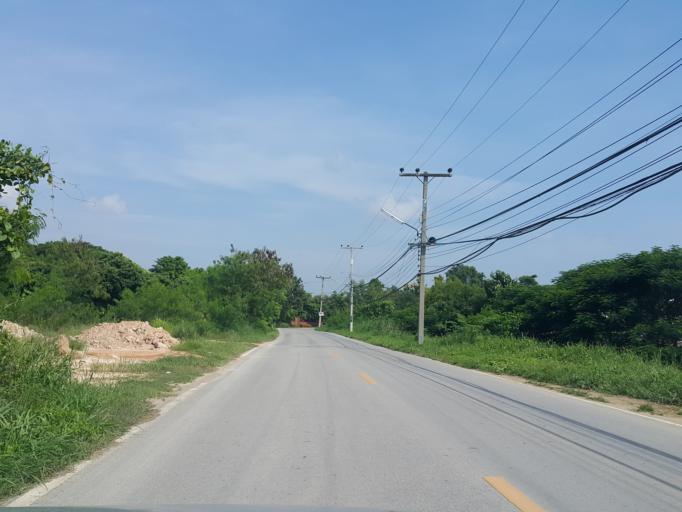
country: TH
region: Chiang Mai
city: Saraphi
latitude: 18.6886
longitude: 99.0605
